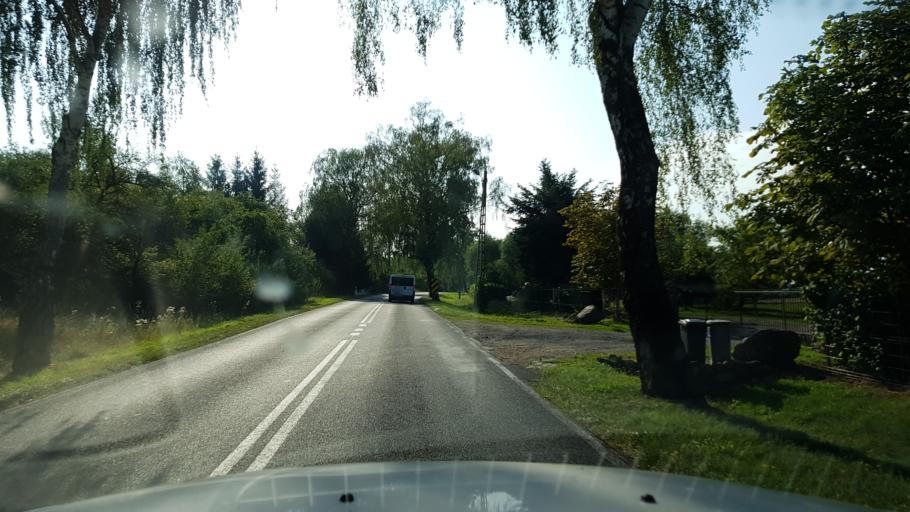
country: PL
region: West Pomeranian Voivodeship
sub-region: Powiat gryficki
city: Ploty
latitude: 53.7862
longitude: 15.3259
